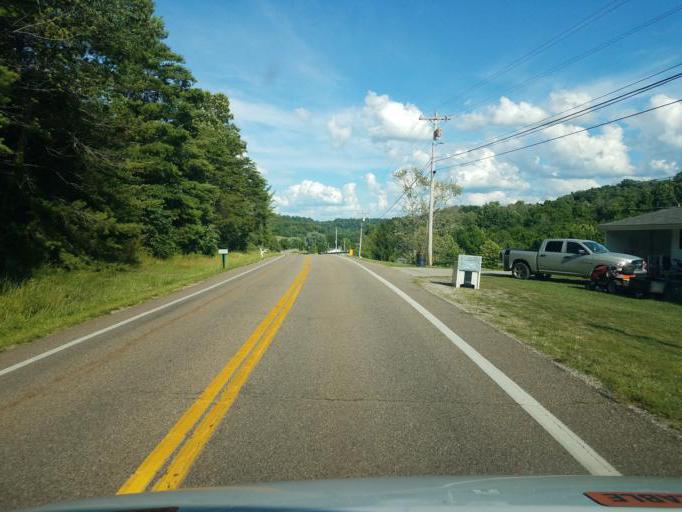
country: US
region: Ohio
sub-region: Gallia County
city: Gallipolis
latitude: 38.8002
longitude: -82.2933
